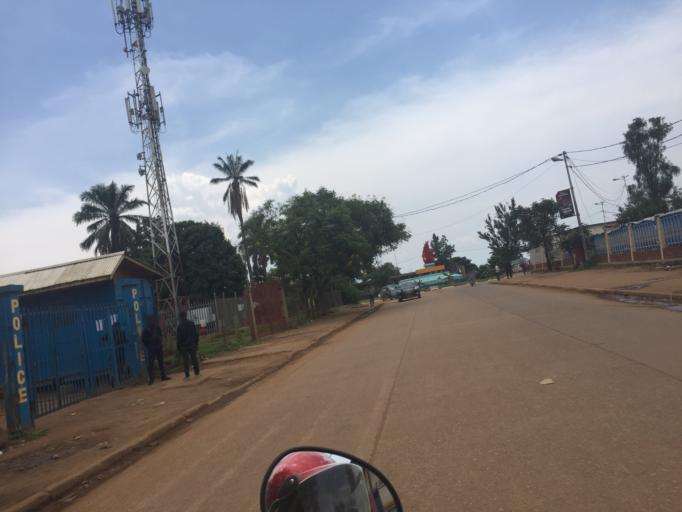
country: CD
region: South Kivu
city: Bukavu
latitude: -2.4882
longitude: 28.8561
